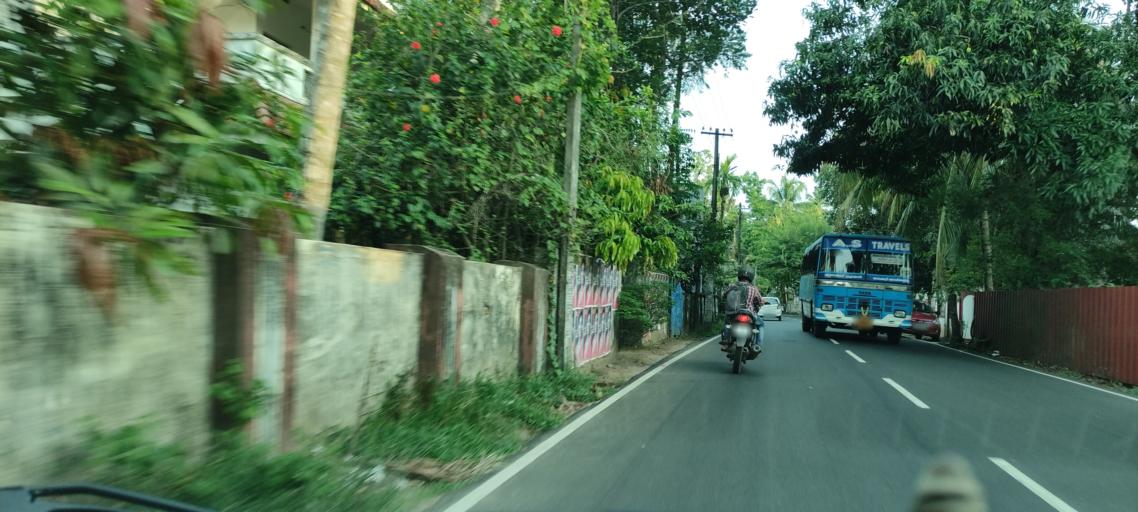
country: IN
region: Kerala
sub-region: Alappuzha
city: Arukutti
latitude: 9.8669
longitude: 76.3239
